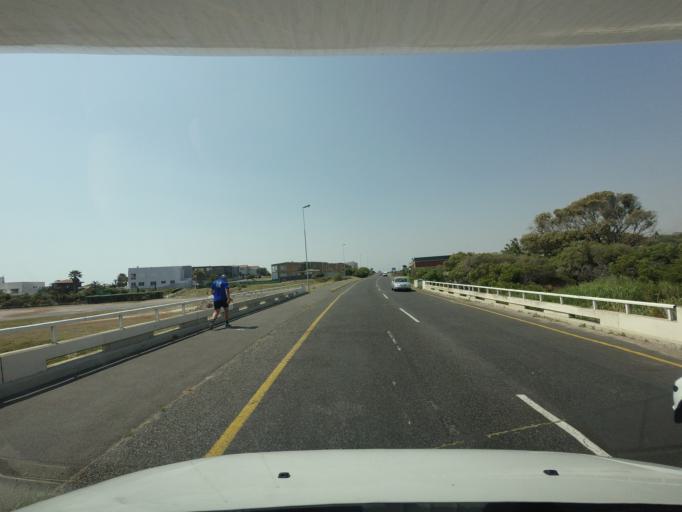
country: ZA
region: Western Cape
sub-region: City of Cape Town
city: Sunset Beach
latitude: -33.7133
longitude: 18.4456
